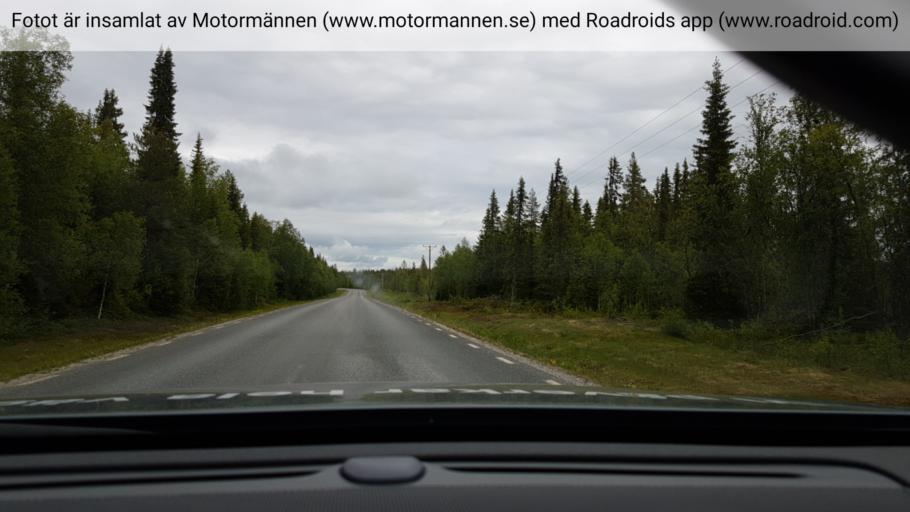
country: SE
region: Vaesterbotten
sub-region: Lycksele Kommun
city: Soderfors
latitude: 64.3648
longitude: 17.9513
